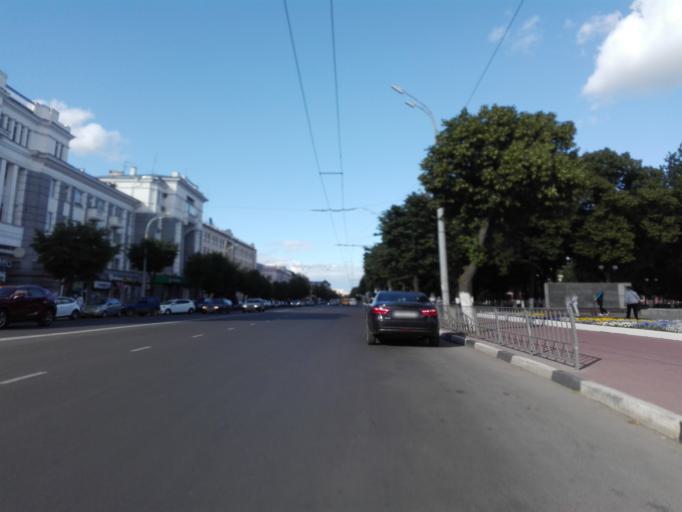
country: RU
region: Orjol
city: Orel
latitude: 52.9677
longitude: 36.0765
